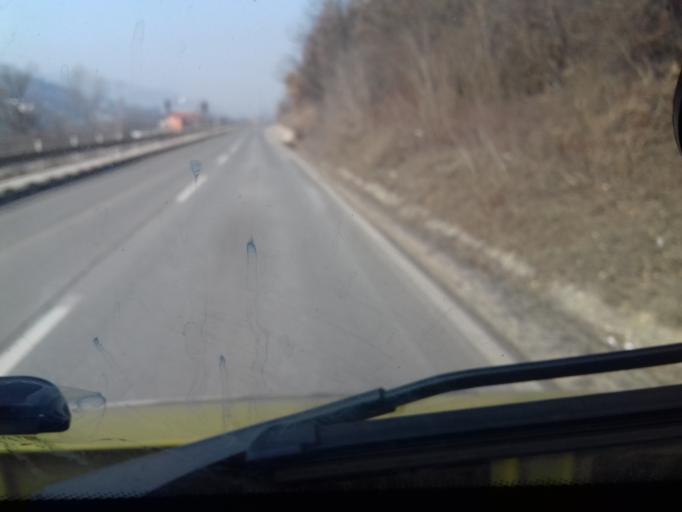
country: BA
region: Federation of Bosnia and Herzegovina
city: Vogosca
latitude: 43.9093
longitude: 18.3261
